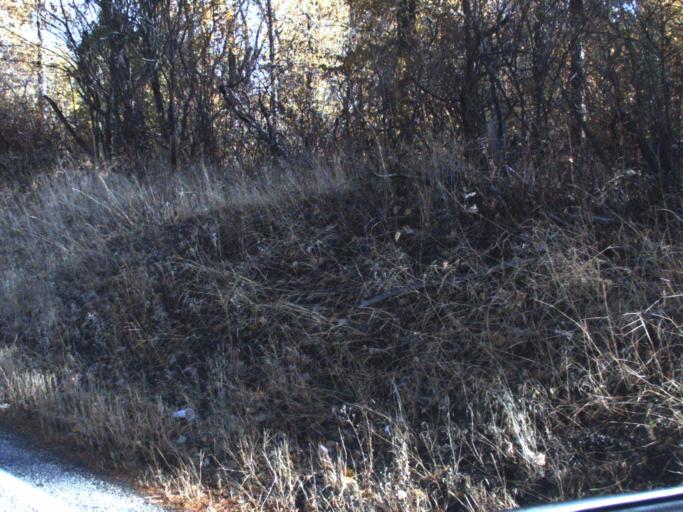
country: CA
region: British Columbia
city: Grand Forks
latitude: 48.9860
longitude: -118.5142
